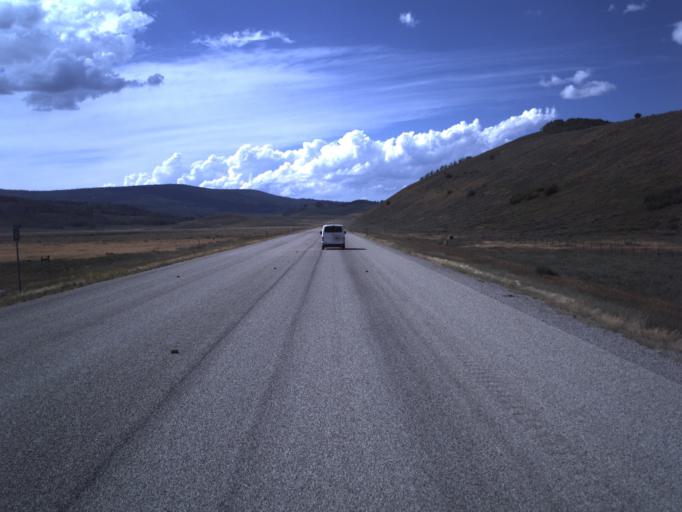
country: US
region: Utah
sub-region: Wasatch County
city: Heber
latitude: 40.2545
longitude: -111.1987
